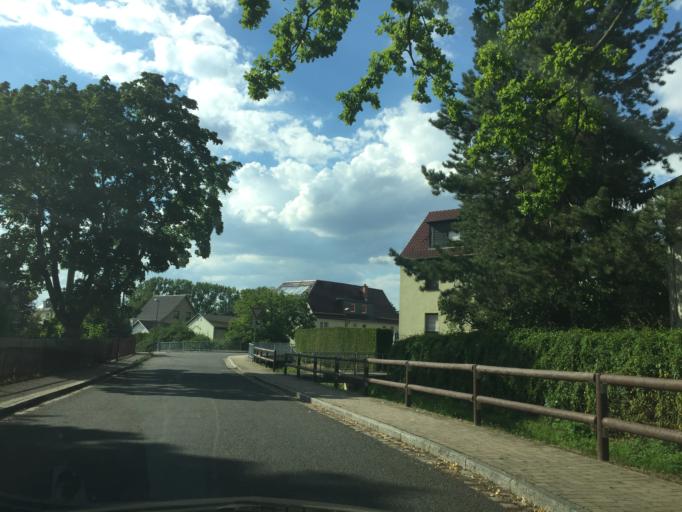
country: DE
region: Thuringia
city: Nobitz
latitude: 50.9757
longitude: 12.4841
